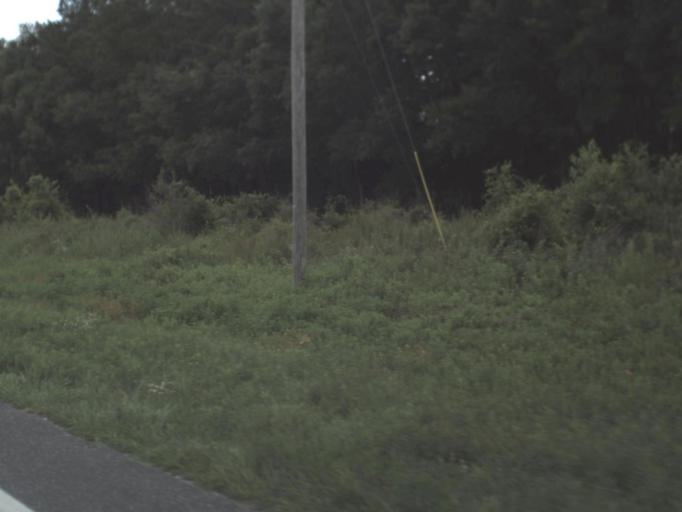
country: US
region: Florida
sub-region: Gilchrist County
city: Trenton
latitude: 29.6121
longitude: -82.9108
